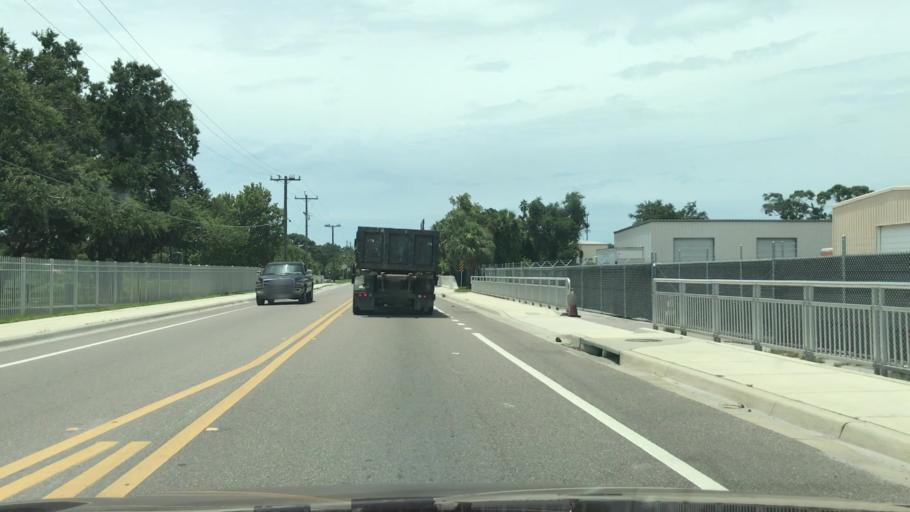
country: US
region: Florida
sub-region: Sarasota County
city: North Sarasota
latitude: 27.3671
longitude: -82.5324
